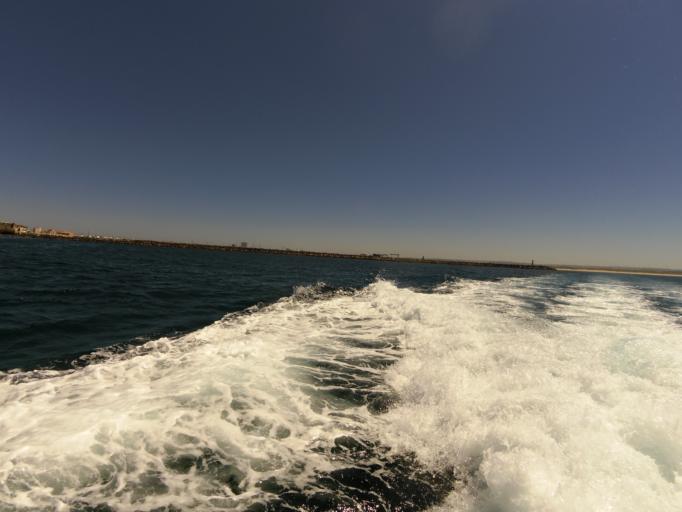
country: PT
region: Leiria
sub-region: Peniche
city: Peniche
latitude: 39.3486
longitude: -9.3817
